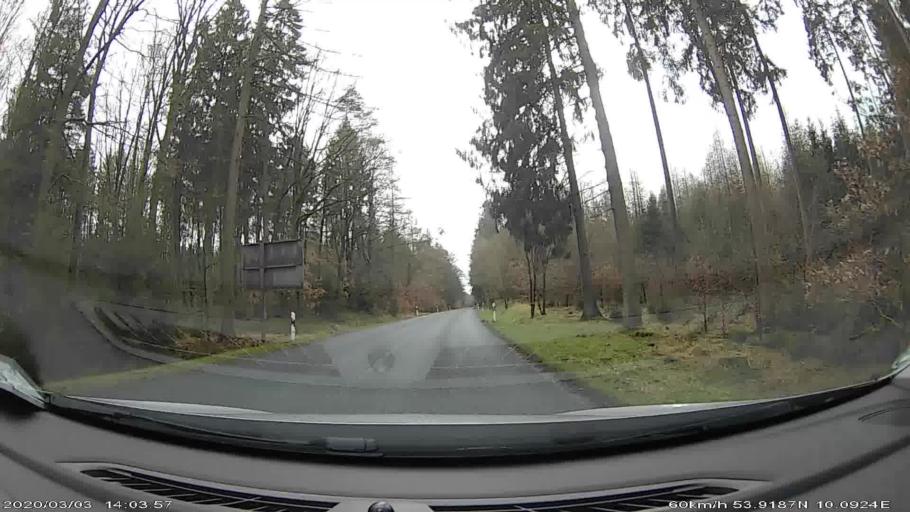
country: DE
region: Schleswig-Holstein
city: Hartenholm
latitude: 53.9180
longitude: 10.0925
